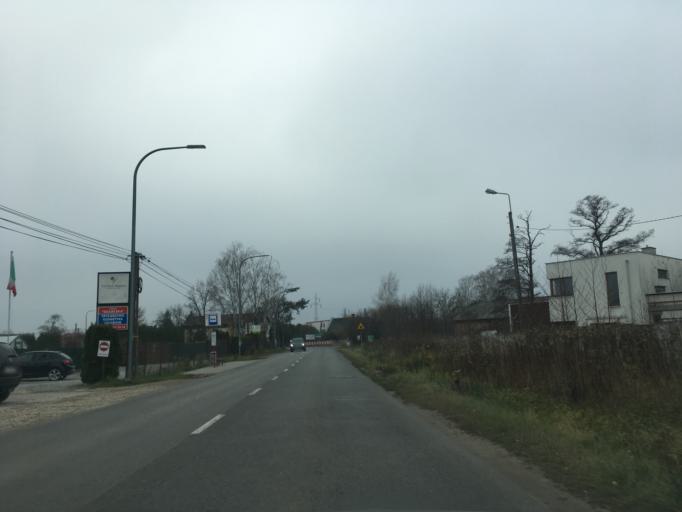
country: PL
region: Masovian Voivodeship
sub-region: Powiat piaseczynski
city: Lesznowola
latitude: 52.0687
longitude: 20.9617
